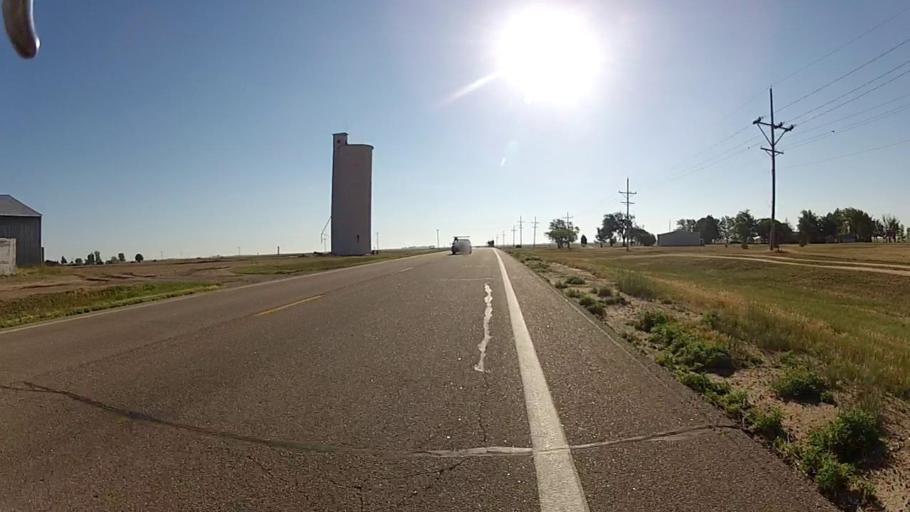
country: US
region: Kansas
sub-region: Haskell County
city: Sublette
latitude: 37.5155
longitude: -100.7277
